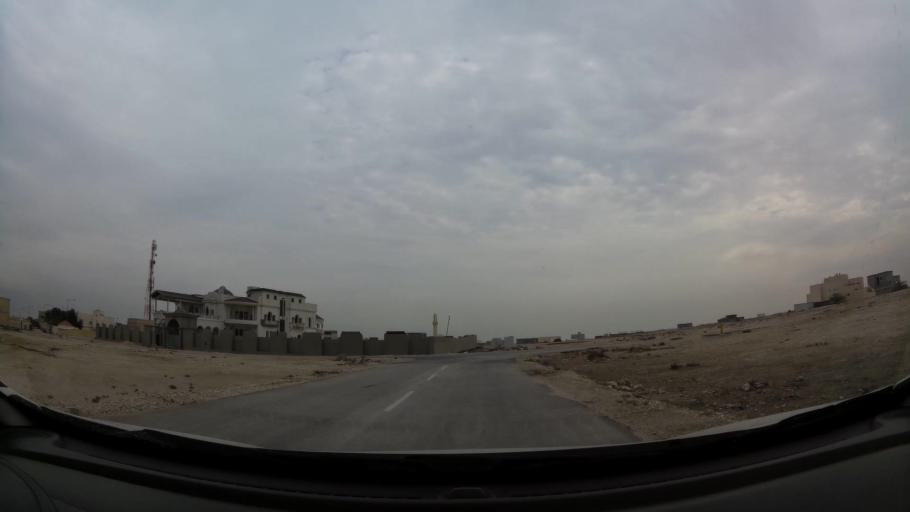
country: BH
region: Northern
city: Ar Rifa'
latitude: 26.0593
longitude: 50.6117
